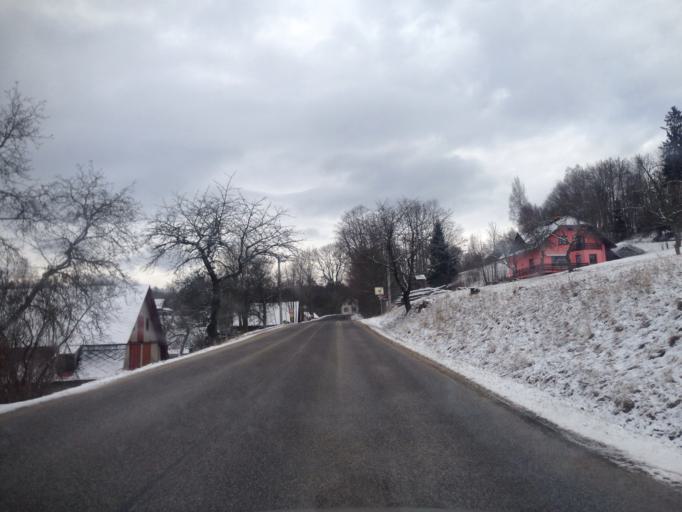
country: CZ
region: Liberecky
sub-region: Okres Semily
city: Vysoke nad Jizerou
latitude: 50.6571
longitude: 15.4160
